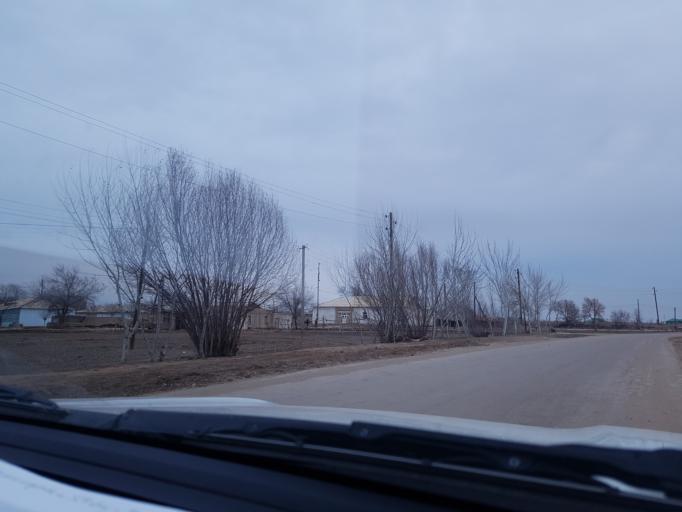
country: TM
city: Akdepe
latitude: 41.9813
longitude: 59.4758
